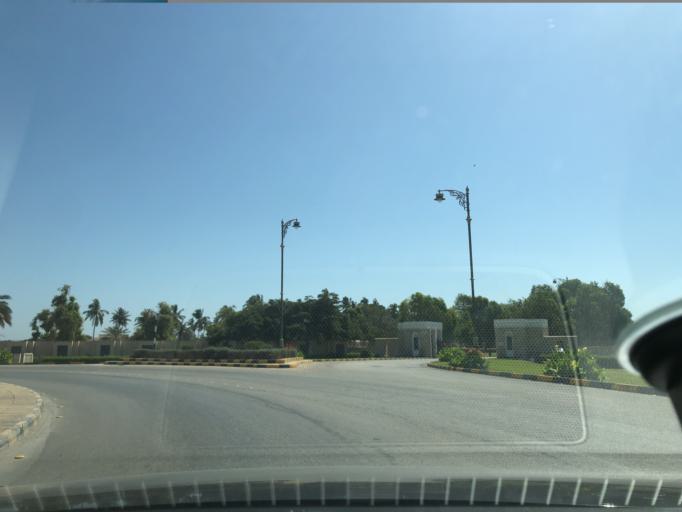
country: OM
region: Zufar
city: Salalah
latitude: 17.0260
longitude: 54.1433
